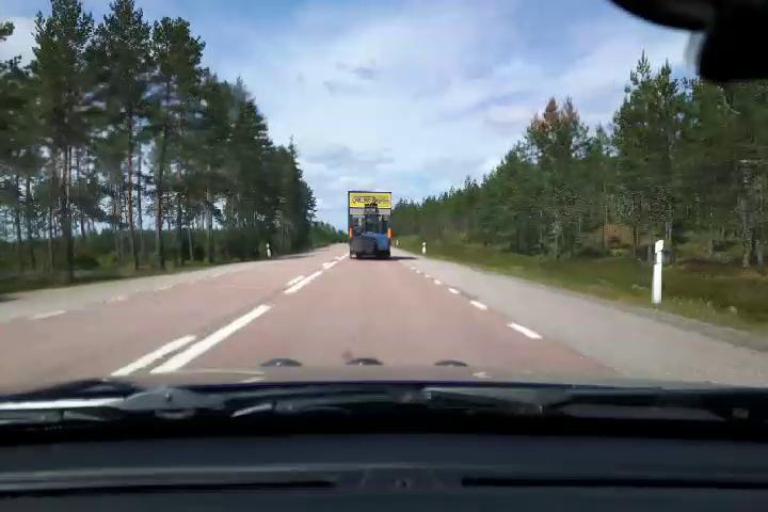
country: SE
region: Uppsala
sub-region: Osthammars Kommun
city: Bjorklinge
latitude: 60.1760
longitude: 17.4840
